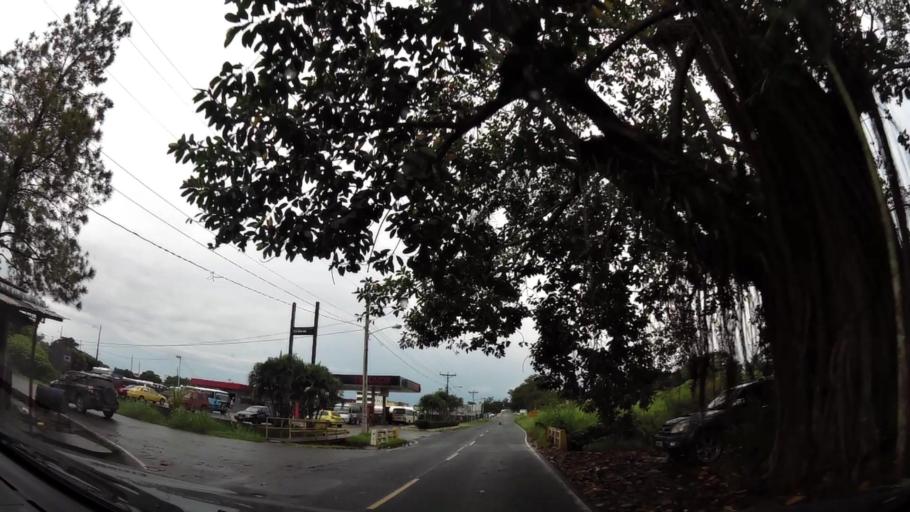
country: PA
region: Veraguas
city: Santiago de Veraguas
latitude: 8.1042
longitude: -80.9761
